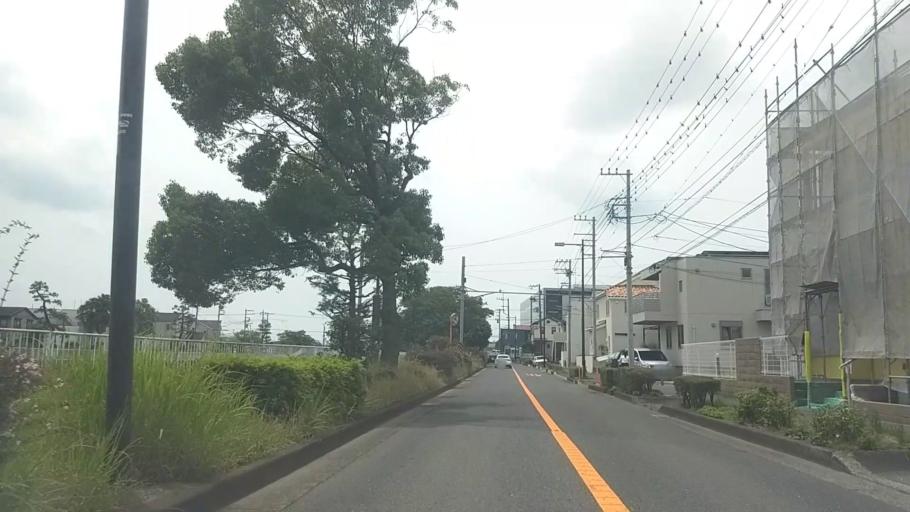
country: JP
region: Kanagawa
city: Fujisawa
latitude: 35.3440
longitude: 139.4665
